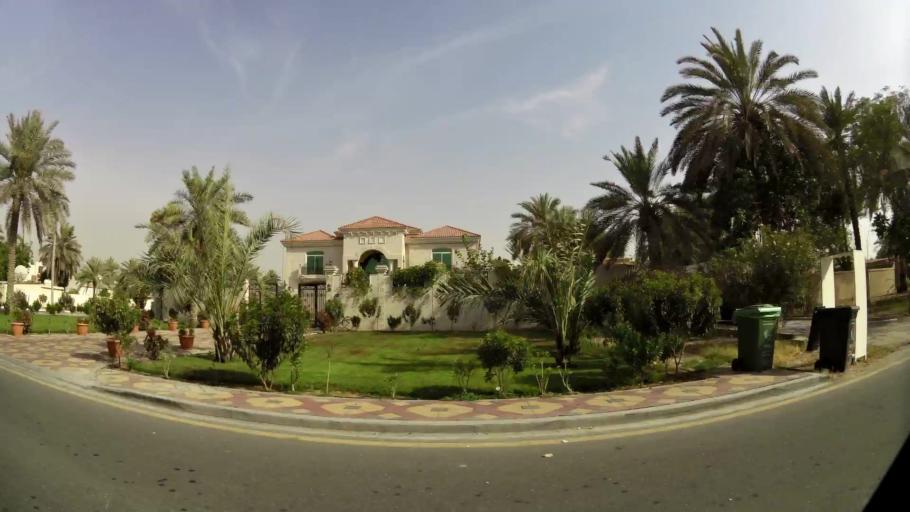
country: AE
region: Ash Shariqah
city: Sharjah
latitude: 25.2520
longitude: 55.4215
